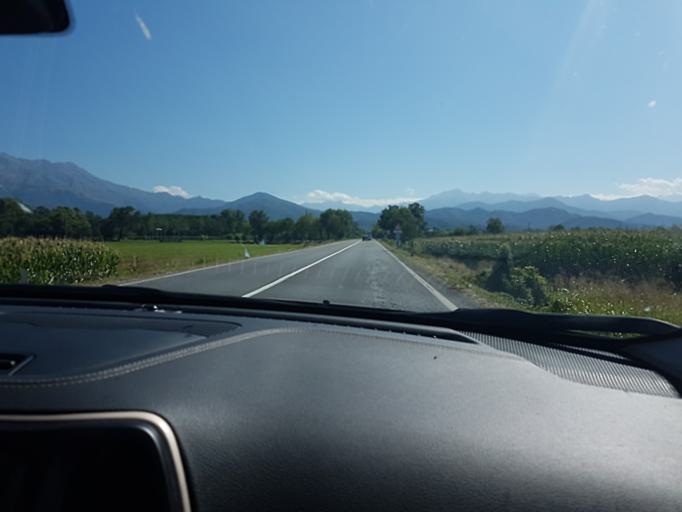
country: IT
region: Piedmont
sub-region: Provincia di Cuneo
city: Cuneo
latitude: 44.3647
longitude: 7.5510
